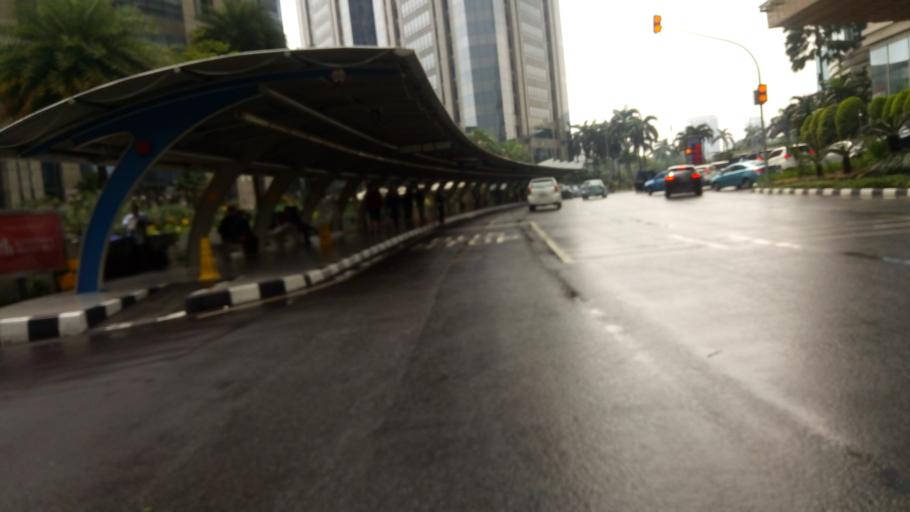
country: ID
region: Jakarta Raya
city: Jakarta
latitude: -6.2249
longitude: 106.8092
